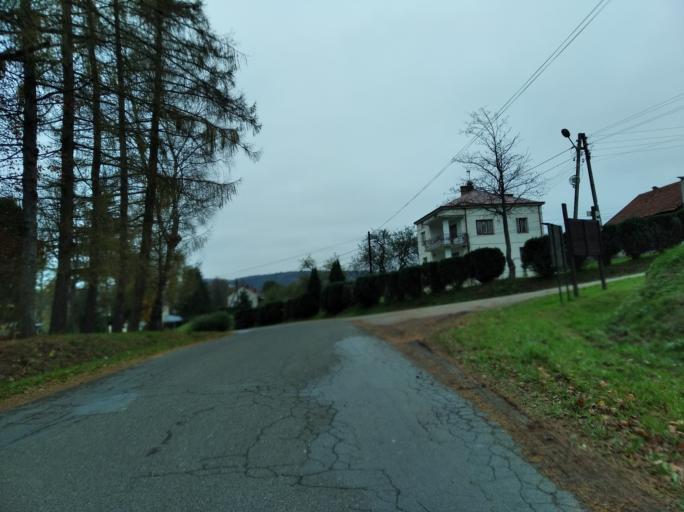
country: PL
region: Subcarpathian Voivodeship
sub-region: Powiat strzyzowski
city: Frysztak
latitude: 49.8371
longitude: 21.6233
